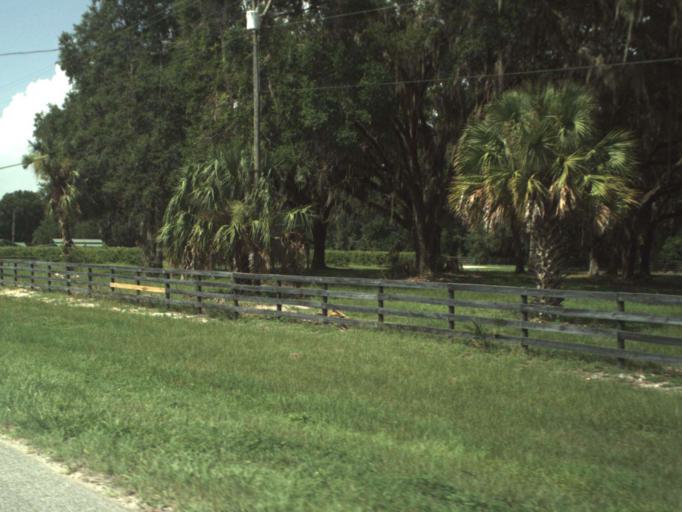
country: US
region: Florida
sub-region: Sumter County
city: Lake Panasoffkee
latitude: 28.7875
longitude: -82.0696
